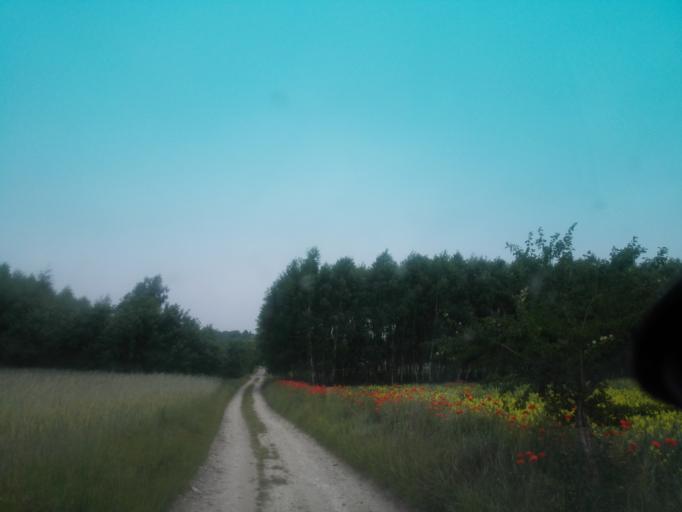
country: PL
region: Silesian Voivodeship
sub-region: Powiat czestochowski
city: Mstow
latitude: 50.7930
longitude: 19.3623
